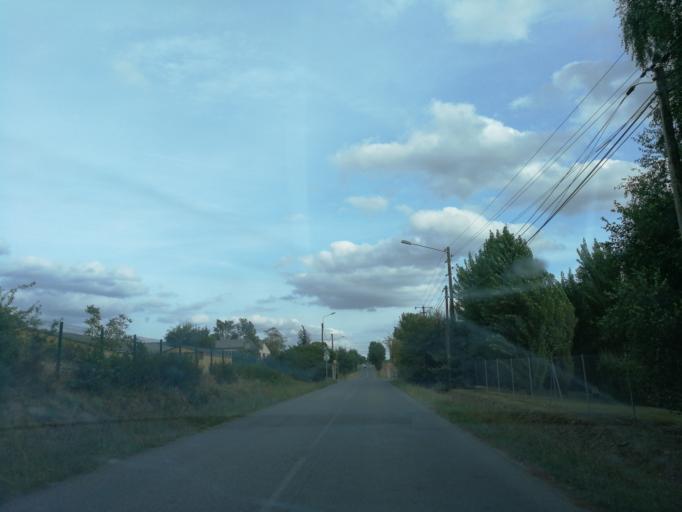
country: FR
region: Midi-Pyrenees
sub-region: Departement de la Haute-Garonne
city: Flourens
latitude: 43.5992
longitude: 1.5464
